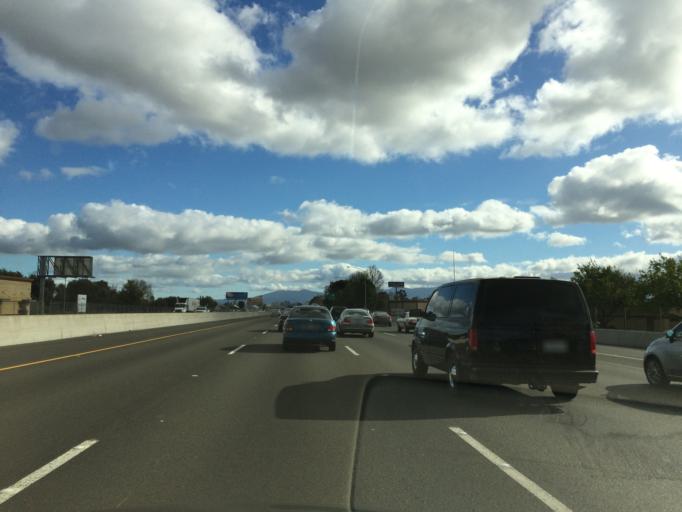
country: US
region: California
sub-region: Santa Clara County
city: San Jose
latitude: 37.3789
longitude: -121.9038
